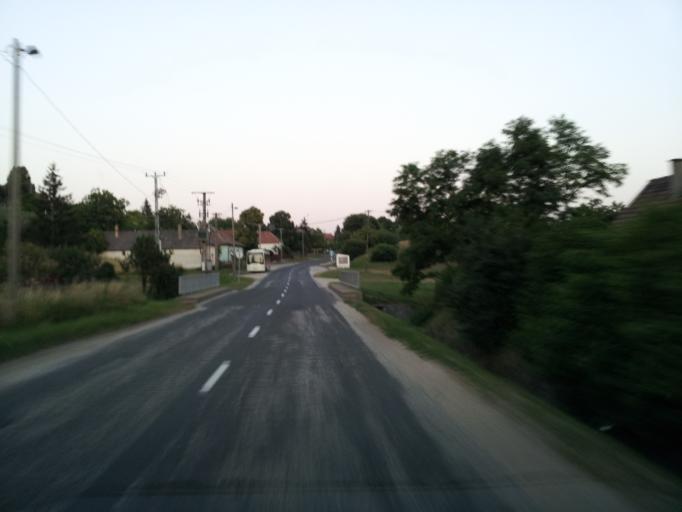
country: HU
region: Fejer
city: Szarliget
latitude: 47.4940
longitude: 18.5654
